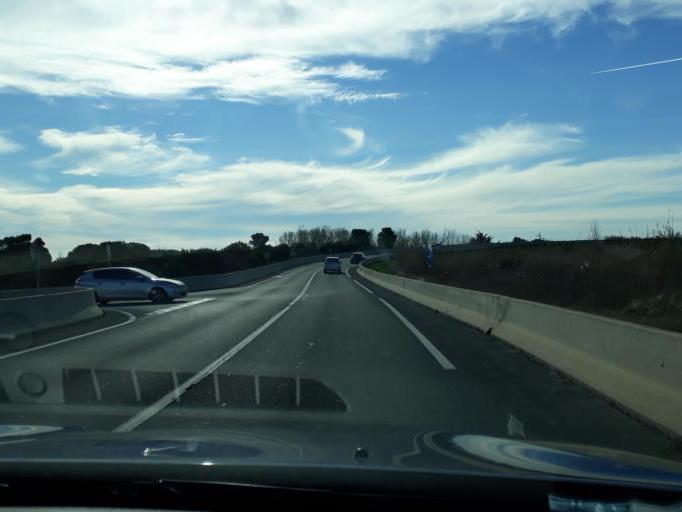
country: FR
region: Languedoc-Roussillon
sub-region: Departement de l'Herault
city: Marseillan
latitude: 43.3204
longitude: 3.5426
